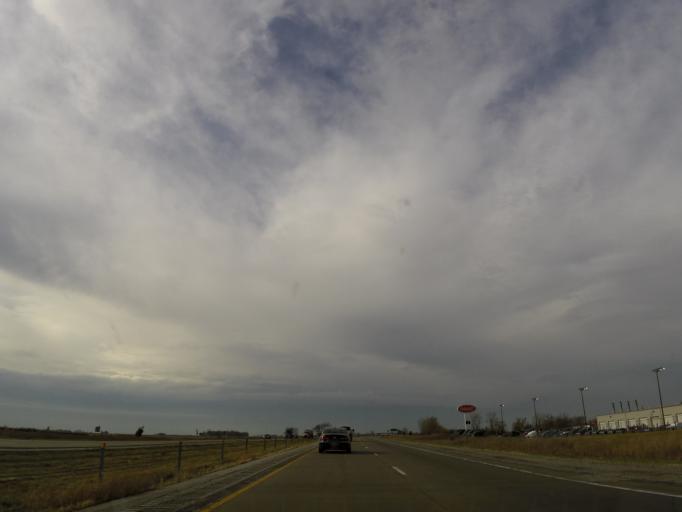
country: US
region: Iowa
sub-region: Scott County
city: Eldridge
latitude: 41.6003
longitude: -90.6283
